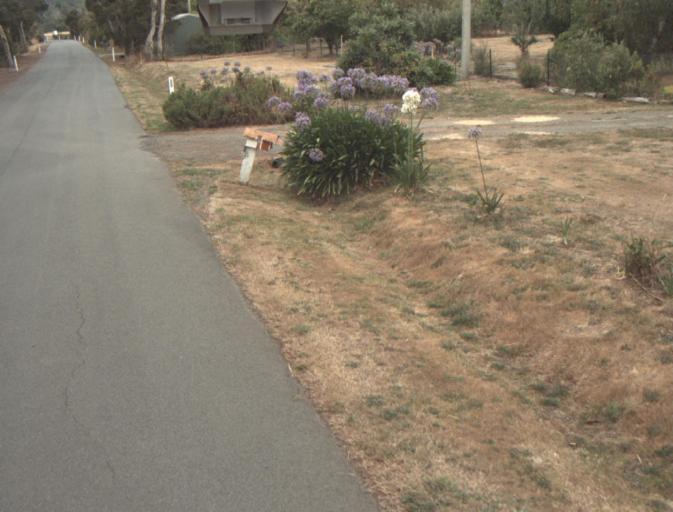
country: AU
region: Tasmania
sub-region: Launceston
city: Mayfield
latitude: -41.2849
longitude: 147.0010
